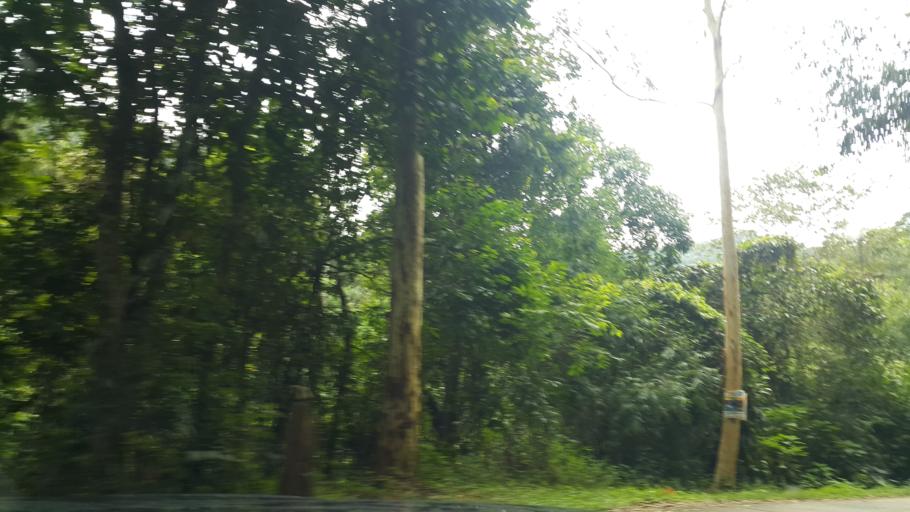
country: TH
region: Lampang
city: Wang Nuea
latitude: 19.0846
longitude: 99.3778
